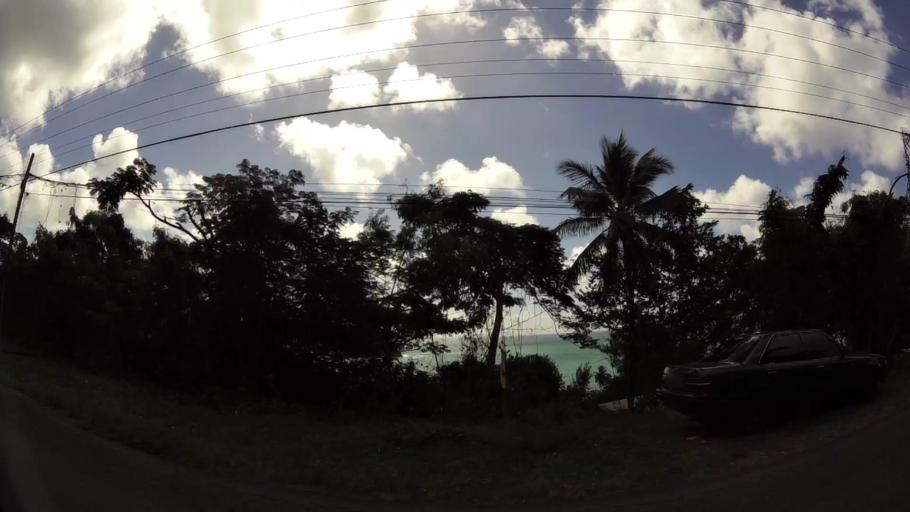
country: LC
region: Laborie Quarter
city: Laborie
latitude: 13.7537
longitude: -60.9996
